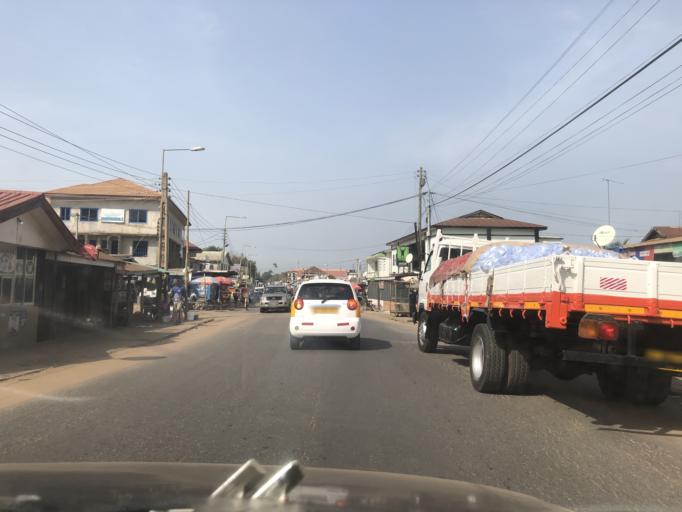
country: GH
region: Eastern
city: Koforidua
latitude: 6.0953
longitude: -0.2592
